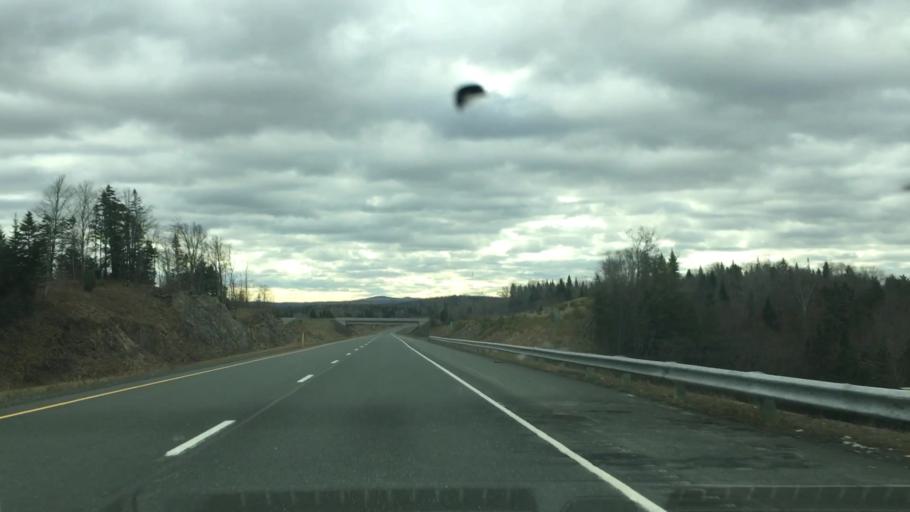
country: US
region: Maine
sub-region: Aroostook County
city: Easton
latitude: 46.6299
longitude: -67.7414
